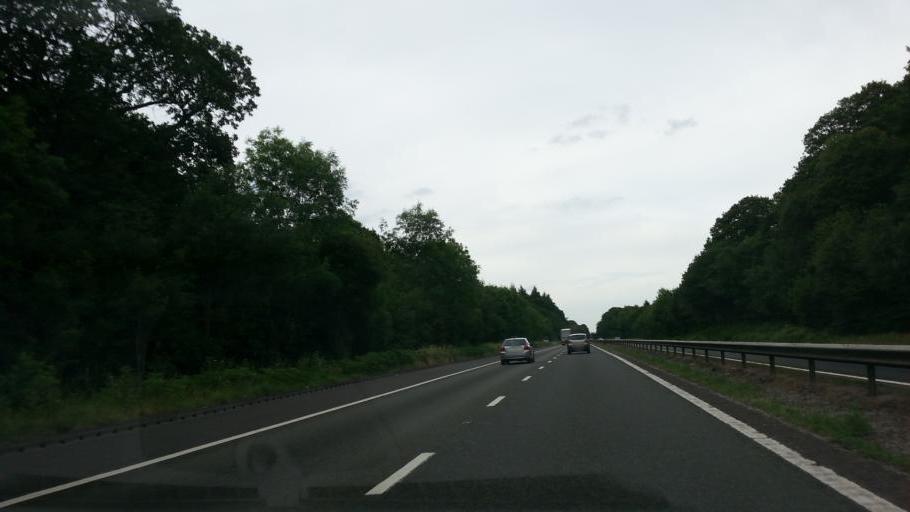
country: GB
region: England
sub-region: Herefordshire
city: Linton
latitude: 51.9488
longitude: -2.4548
